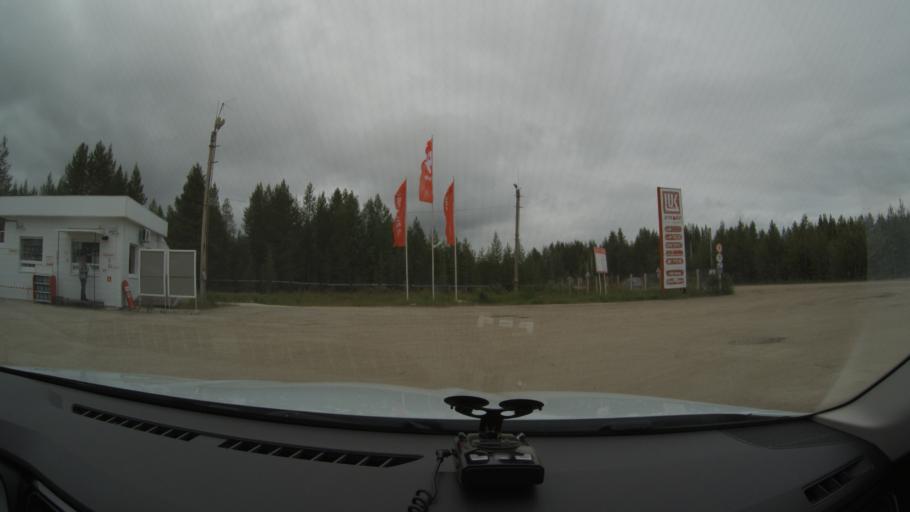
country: RU
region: Komi Republic
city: Kozhva
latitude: 65.1164
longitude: 56.9996
